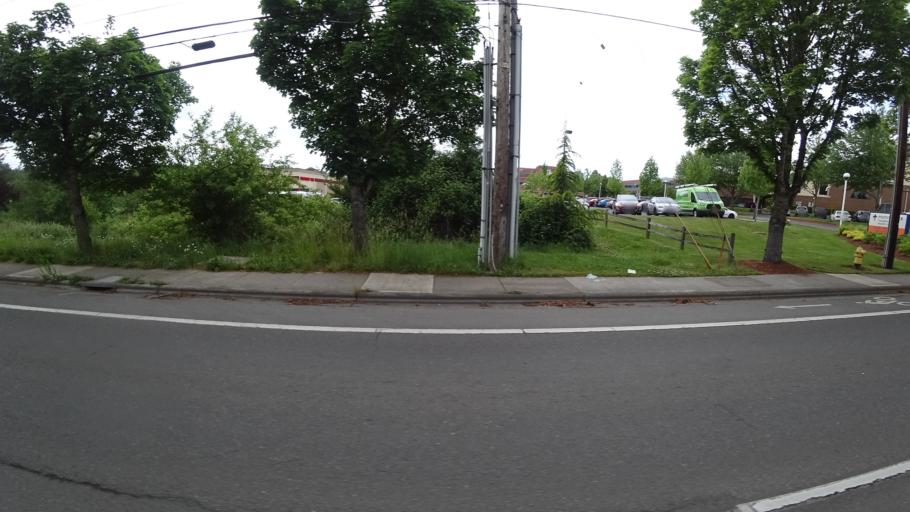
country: US
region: Oregon
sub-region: Washington County
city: Rockcreek
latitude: 45.5328
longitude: -122.8675
